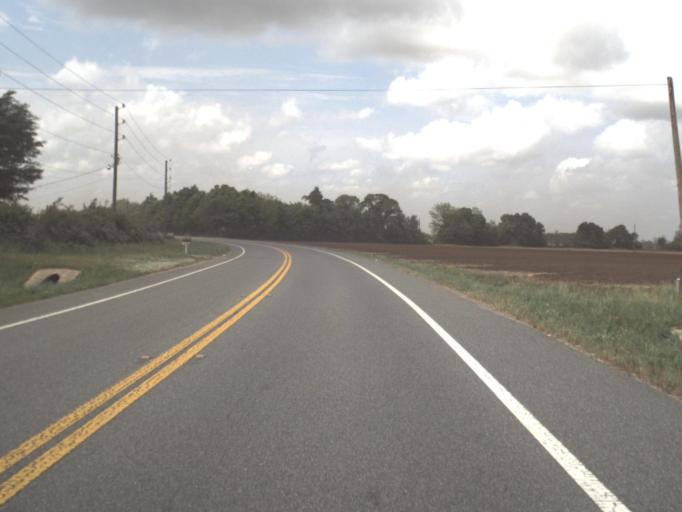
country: US
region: Florida
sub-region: Santa Rosa County
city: Point Baker
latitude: 30.8032
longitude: -87.0938
